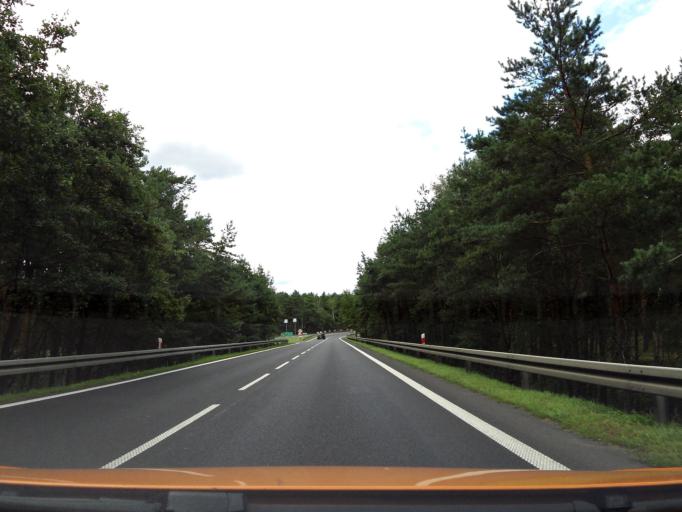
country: PL
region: West Pomeranian Voivodeship
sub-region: Powiat stargardzki
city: Kobylanka
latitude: 53.4262
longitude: 14.7721
